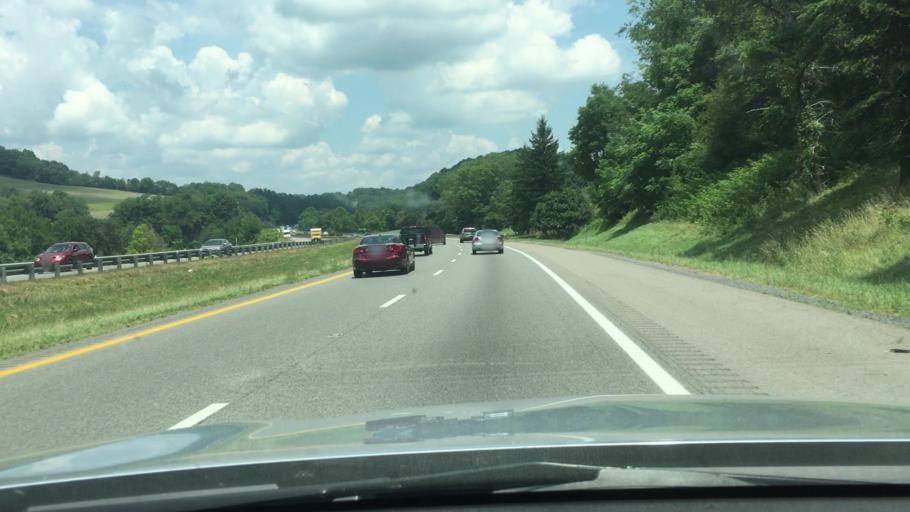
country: US
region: Virginia
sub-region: Smyth County
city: Atkins
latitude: 36.8718
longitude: -81.4013
